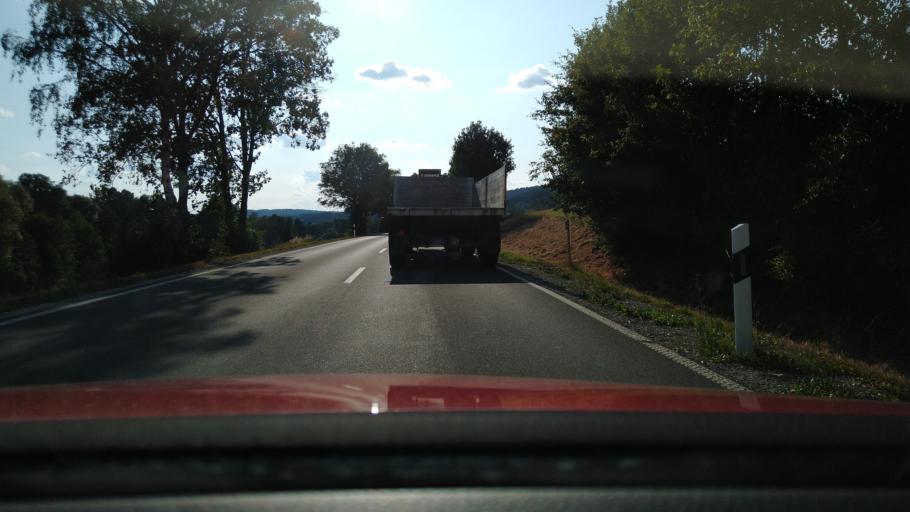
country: DE
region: Bavaria
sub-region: Upper Franconia
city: Mistelgau
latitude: 49.9227
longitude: 11.4296
